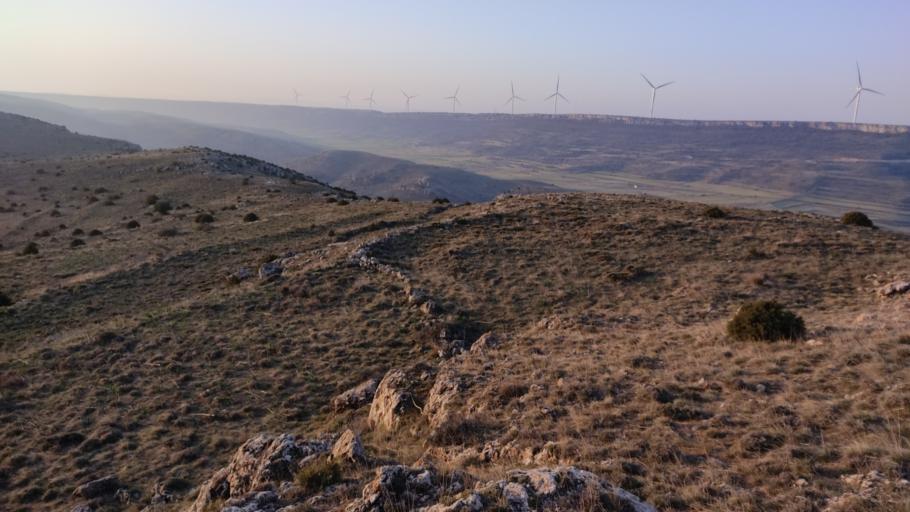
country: ES
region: Aragon
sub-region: Provincia de Teruel
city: Allueva
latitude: 41.0190
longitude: -1.0438
